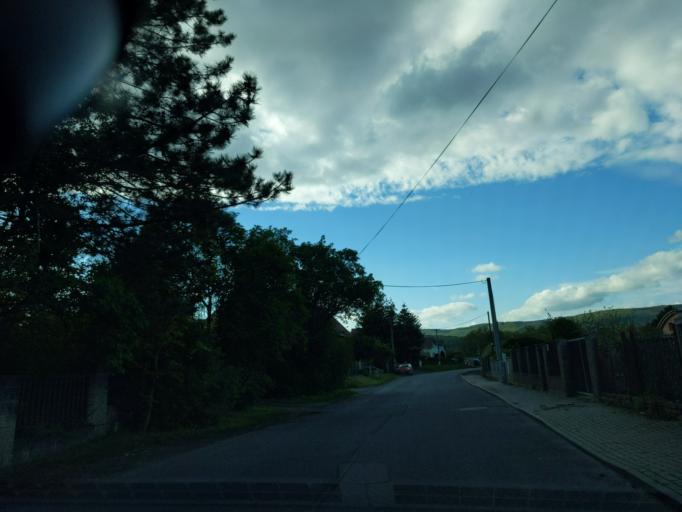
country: CZ
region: Ustecky
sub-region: Okres Usti nad Labem
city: Usti nad Labem
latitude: 50.6911
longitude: 14.0046
